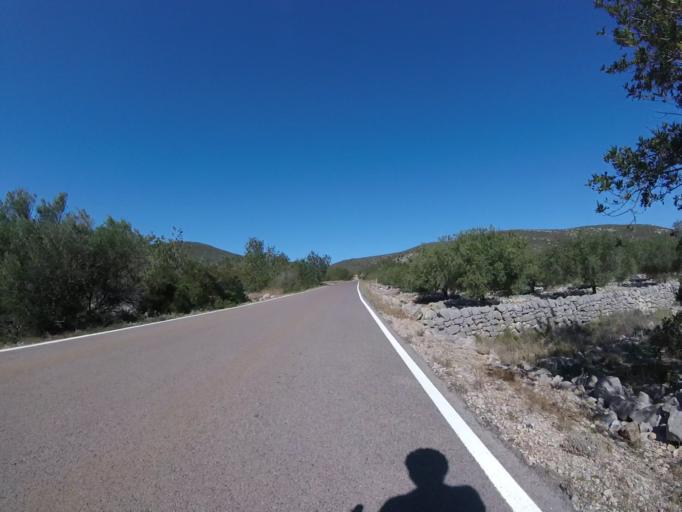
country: ES
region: Valencia
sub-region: Provincia de Castello
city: Santa Magdalena de Pulpis
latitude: 40.3809
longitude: 0.2645
